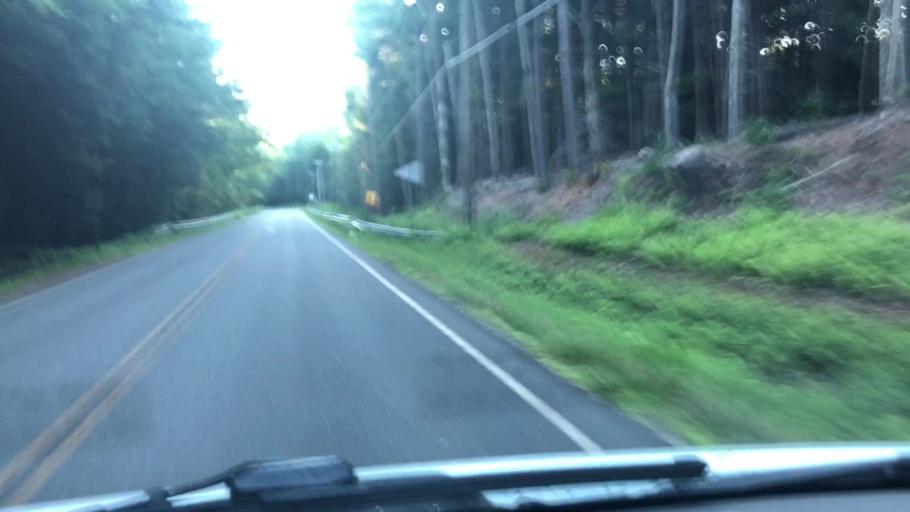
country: US
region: Massachusetts
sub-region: Berkshire County
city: Hinsdale
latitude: 42.4683
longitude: -72.9870
